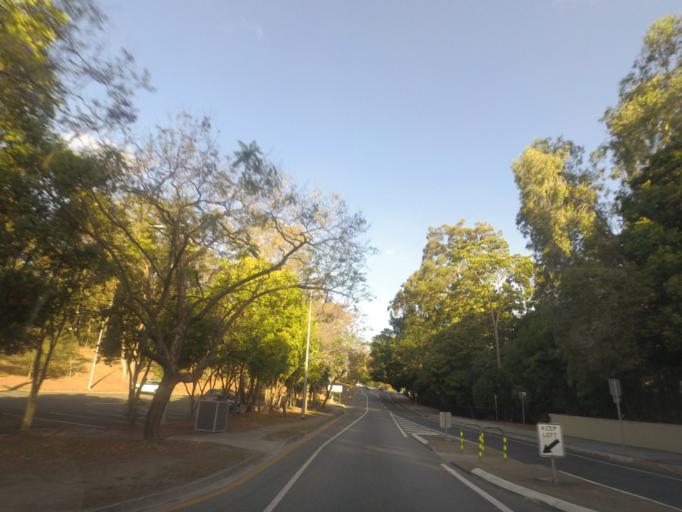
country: AU
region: Queensland
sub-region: Brisbane
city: Toowong
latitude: -27.4743
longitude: 152.9774
